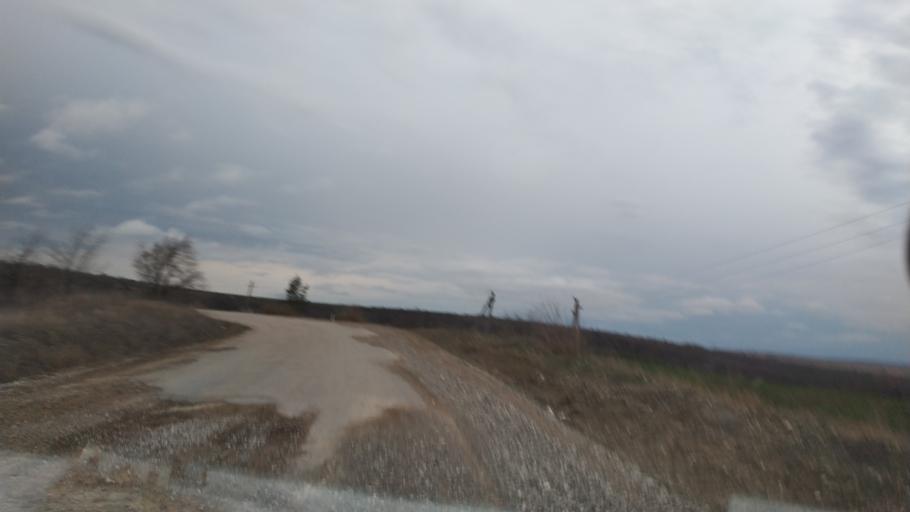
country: MD
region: Causeni
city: Causeni
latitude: 46.6163
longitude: 29.3951
